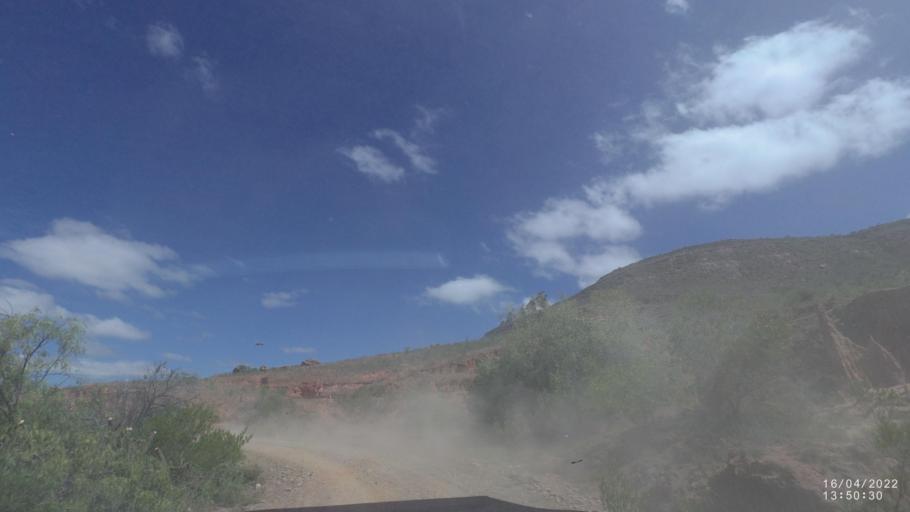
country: BO
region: Cochabamba
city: Mizque
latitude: -18.0162
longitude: -65.5762
